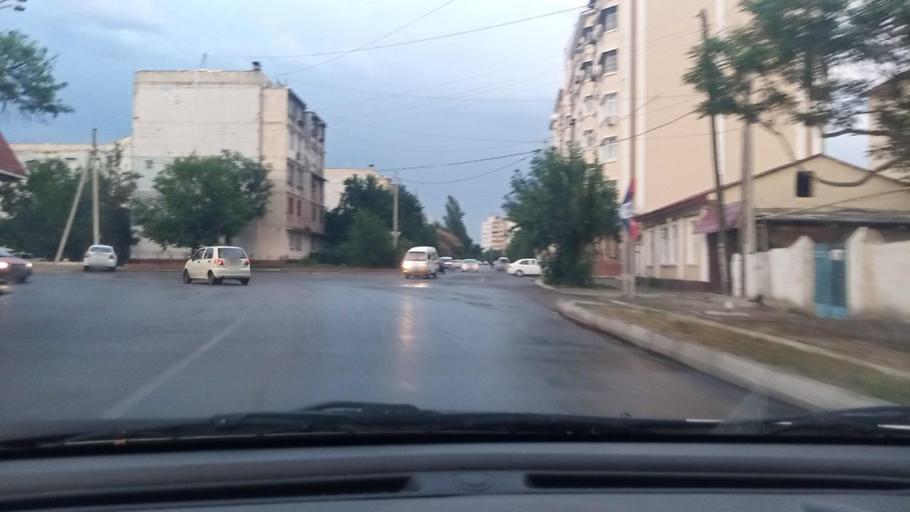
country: UZ
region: Toshkent Shahri
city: Tashkent
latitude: 41.2805
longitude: 69.2855
